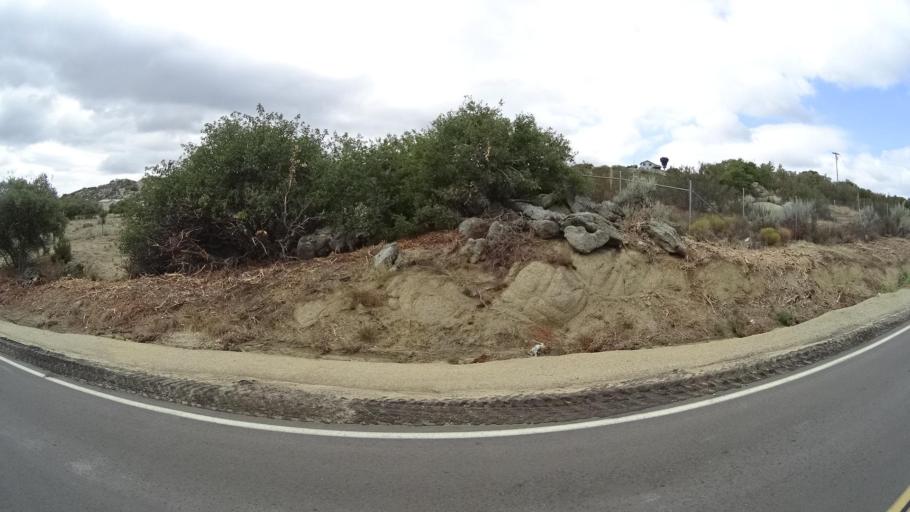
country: US
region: California
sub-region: San Diego County
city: Campo
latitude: 32.6695
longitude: -116.5020
